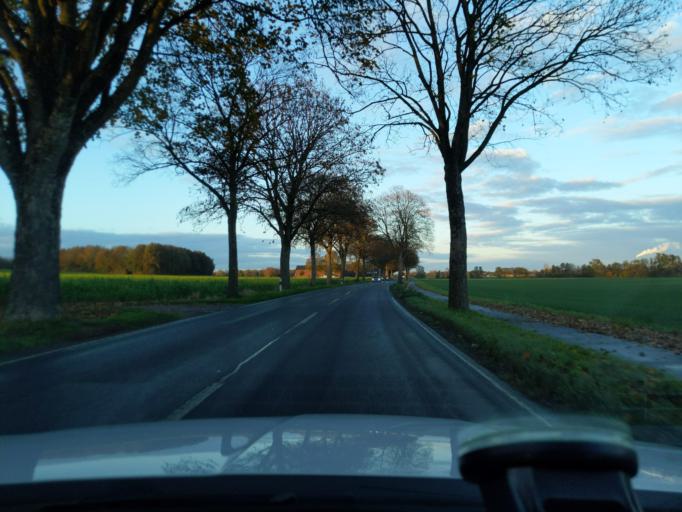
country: DE
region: North Rhine-Westphalia
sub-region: Regierungsbezirk Dusseldorf
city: Uedem
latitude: 51.6944
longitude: 6.3195
